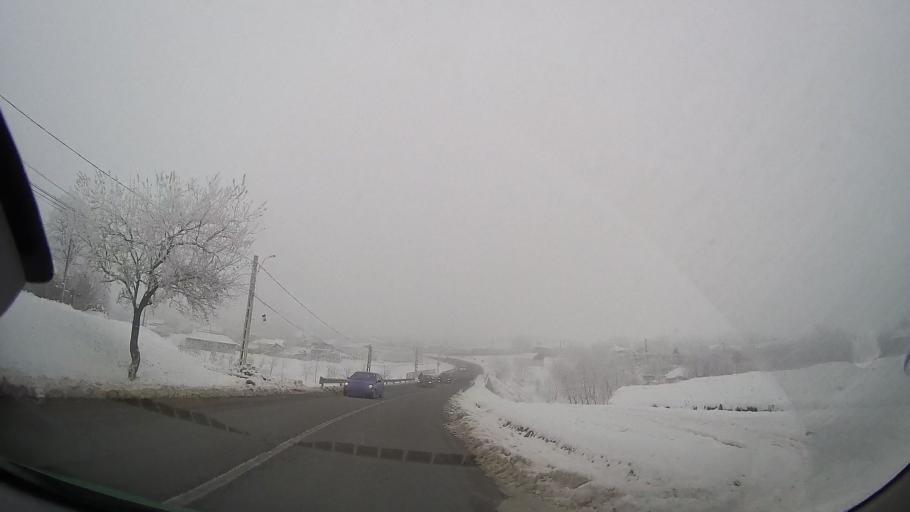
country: RO
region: Iasi
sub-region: Comuna Stolniceni-Prajescu
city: Stolniceni-Prajescu
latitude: 47.1677
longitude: 26.7675
